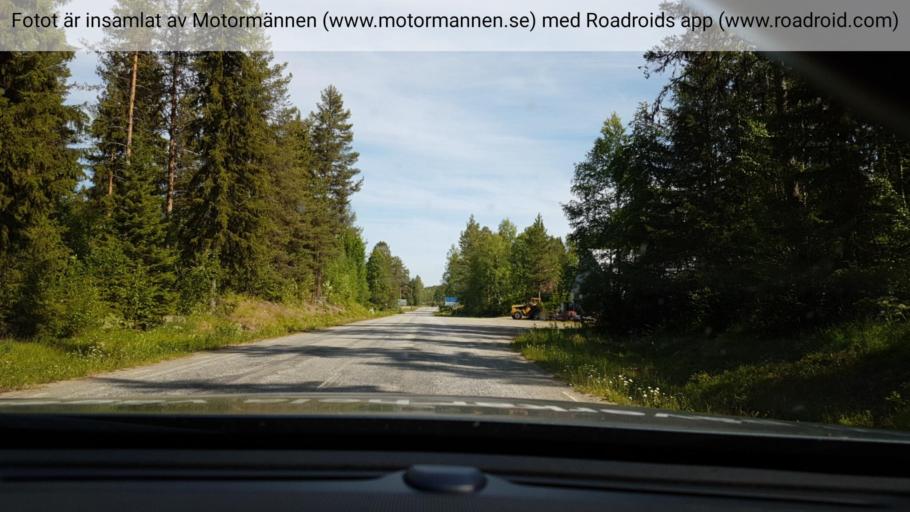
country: SE
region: Vaesterbotten
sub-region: Vilhelmina Kommun
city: Sjoberg
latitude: 64.5725
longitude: 15.8725
